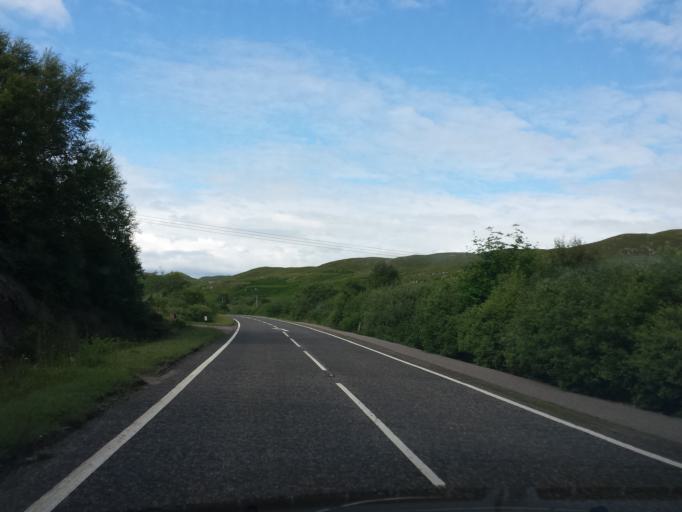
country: GB
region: Scotland
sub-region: Argyll and Bute
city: Isle Of Mull
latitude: 56.9854
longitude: -5.8260
